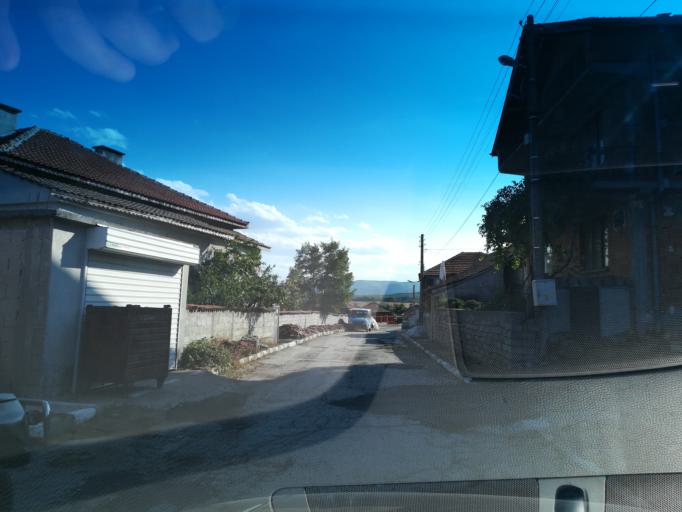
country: BG
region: Khaskovo
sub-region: Obshtina Mineralni Bani
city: Mineralni Bani
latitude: 41.9647
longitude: 25.2937
